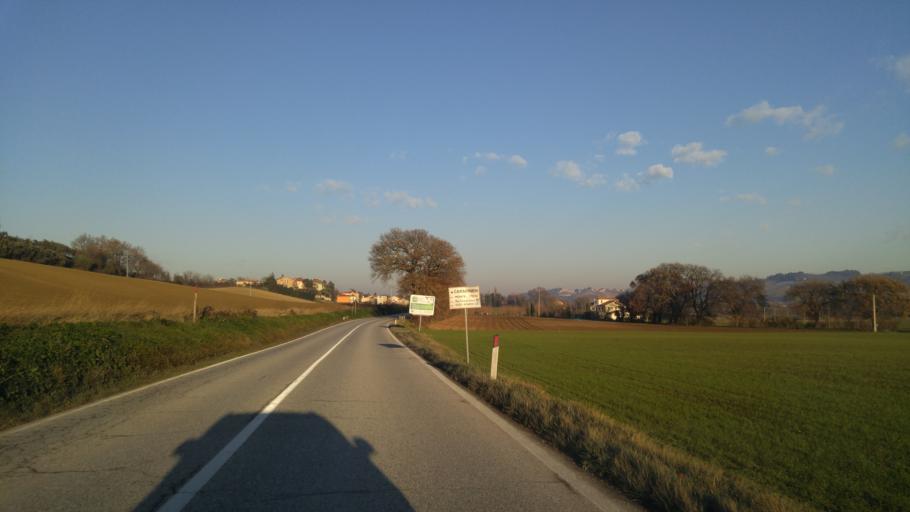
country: IT
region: The Marches
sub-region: Provincia di Pesaro e Urbino
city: Monte Porzio
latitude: 43.6837
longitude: 13.0368
